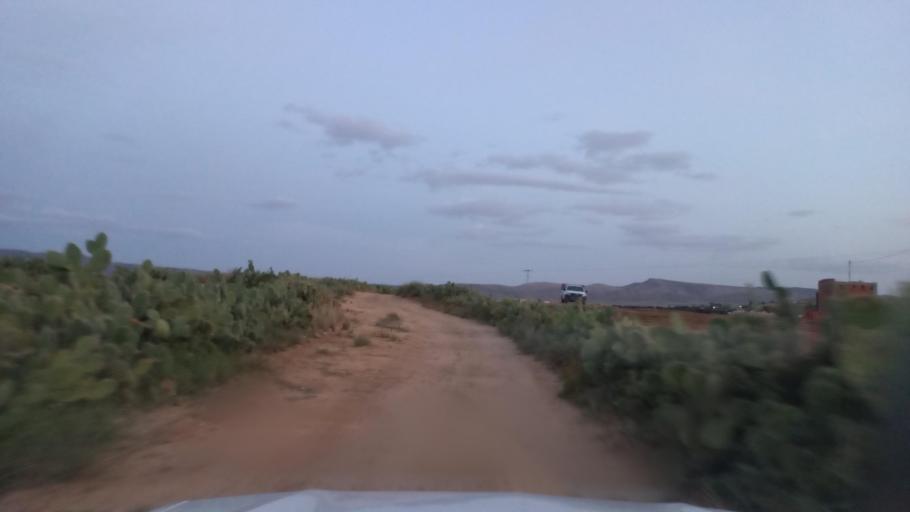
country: TN
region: Al Qasrayn
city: Sbiba
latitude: 35.4208
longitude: 9.1134
